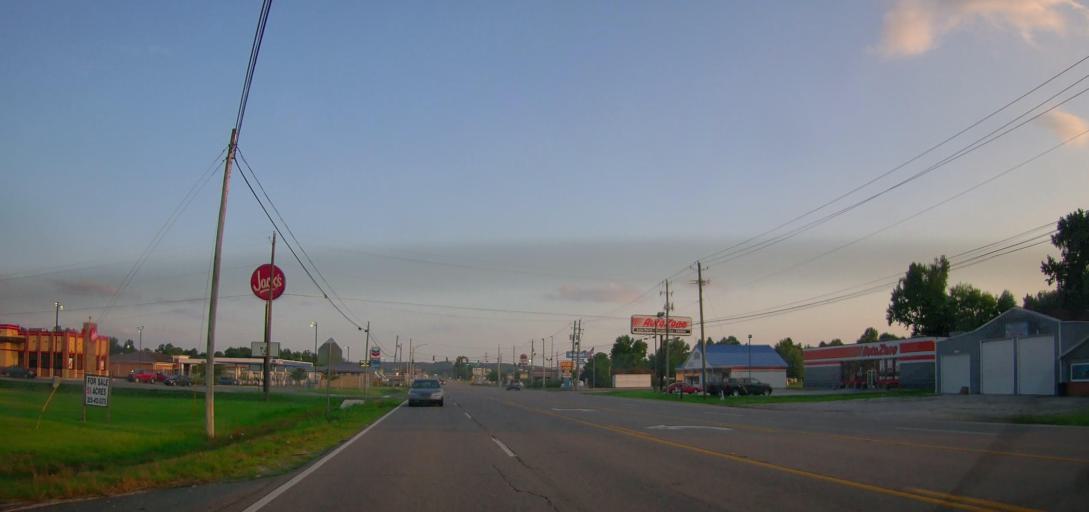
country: US
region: Alabama
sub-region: Marion County
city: Hamilton
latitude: 34.1208
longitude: -87.9896
